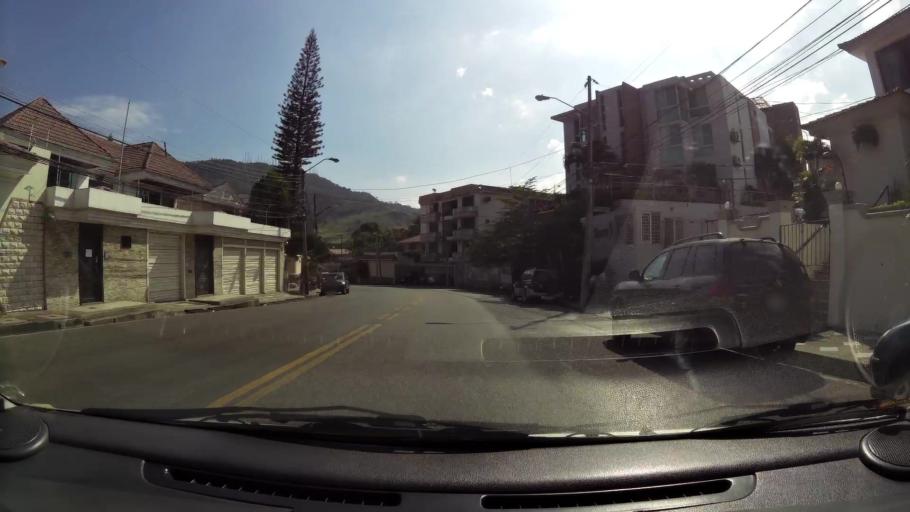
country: EC
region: Guayas
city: Guayaquil
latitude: -2.1614
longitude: -79.9409
